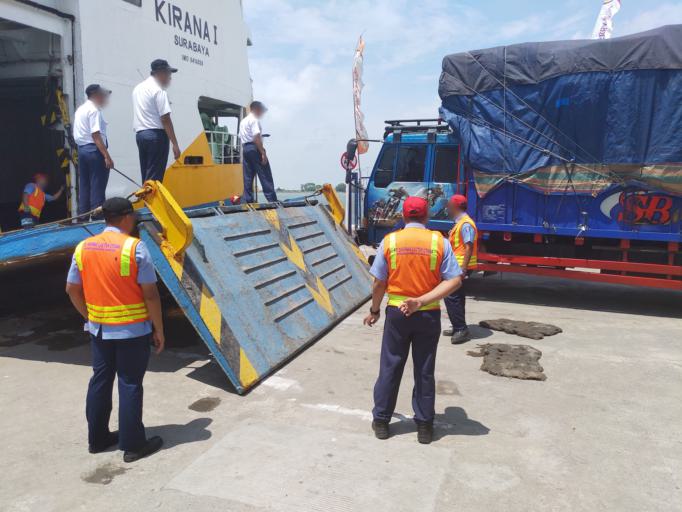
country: ID
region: Central Java
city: Semarang
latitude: -6.9469
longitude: 110.4234
